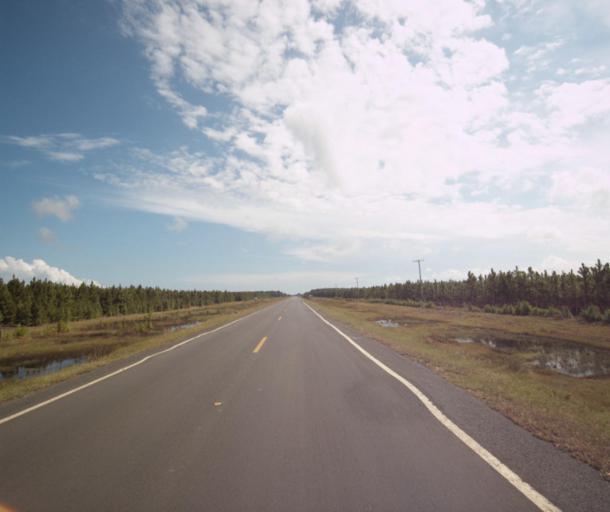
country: BR
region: Rio Grande do Sul
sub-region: Sao Lourenco Do Sul
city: Sao Lourenco do Sul
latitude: -31.5945
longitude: -51.3732
